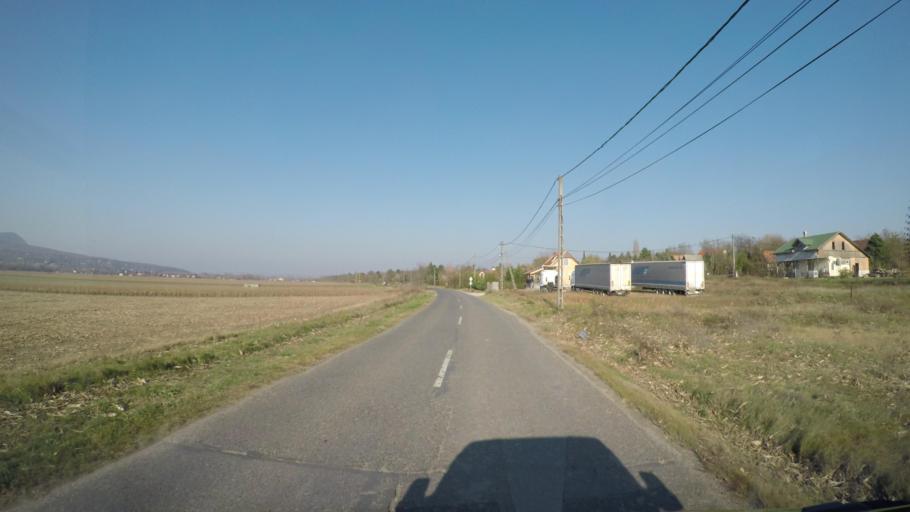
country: HU
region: Pest
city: Leanyfalu
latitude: 47.7032
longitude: 19.1068
